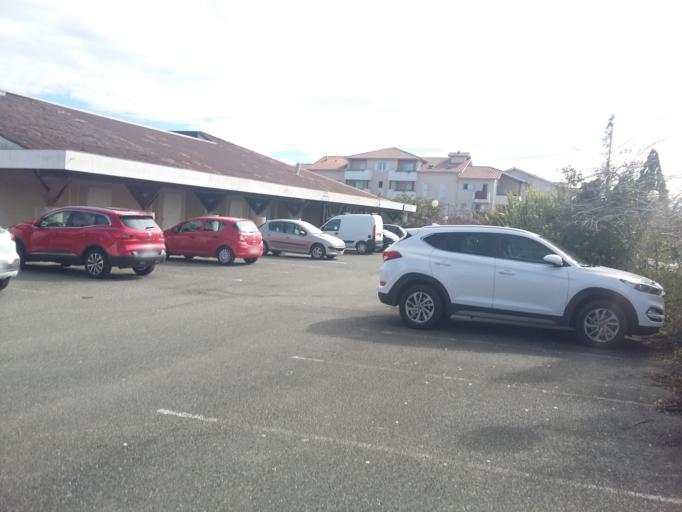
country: FR
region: Aquitaine
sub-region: Departement des Landes
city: Saint-Martin-de-Seignanx
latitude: 43.5421
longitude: -1.3872
